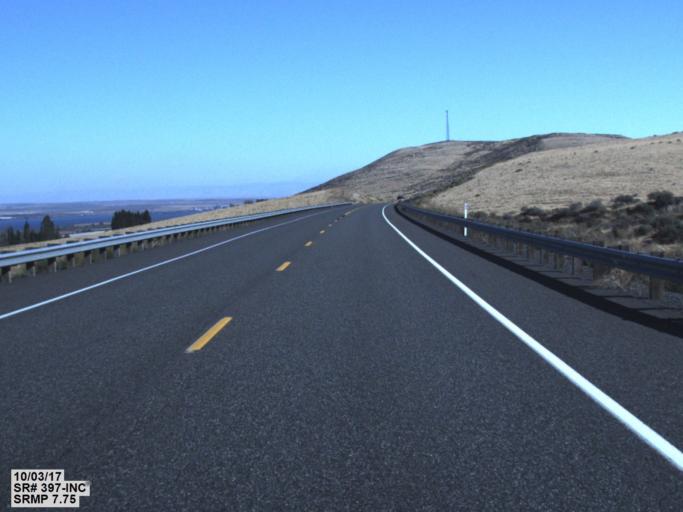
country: US
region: Washington
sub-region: Benton County
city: Finley
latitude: 46.1248
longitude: -119.0564
